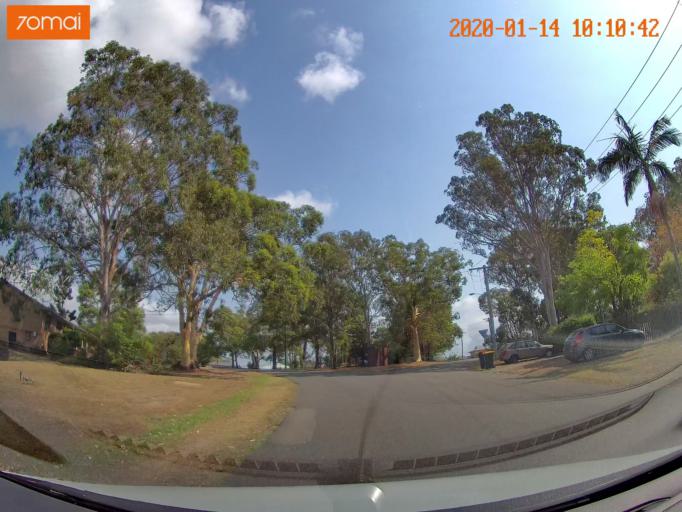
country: AU
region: New South Wales
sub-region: Wyong Shire
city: Kingfisher Shores
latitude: -33.1211
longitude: 151.5360
